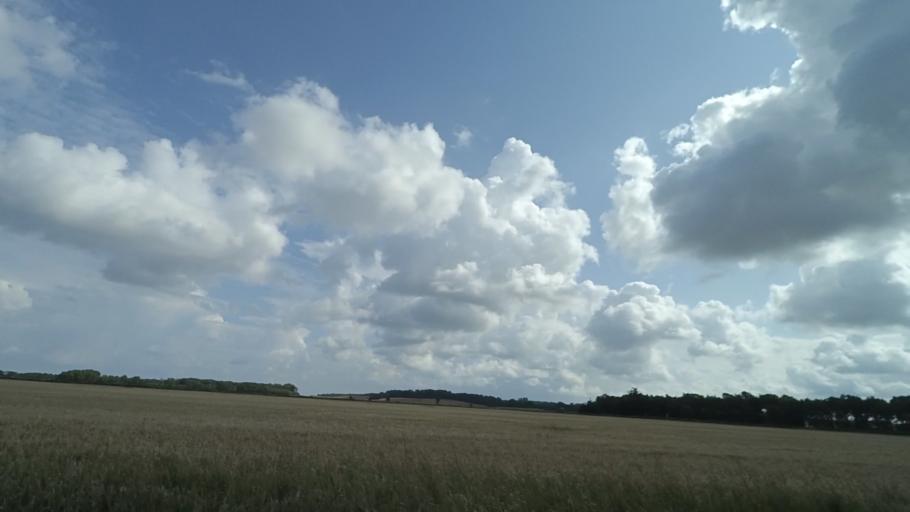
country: DK
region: Central Jutland
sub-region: Norddjurs Kommune
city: Auning
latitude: 56.5058
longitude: 10.4230
